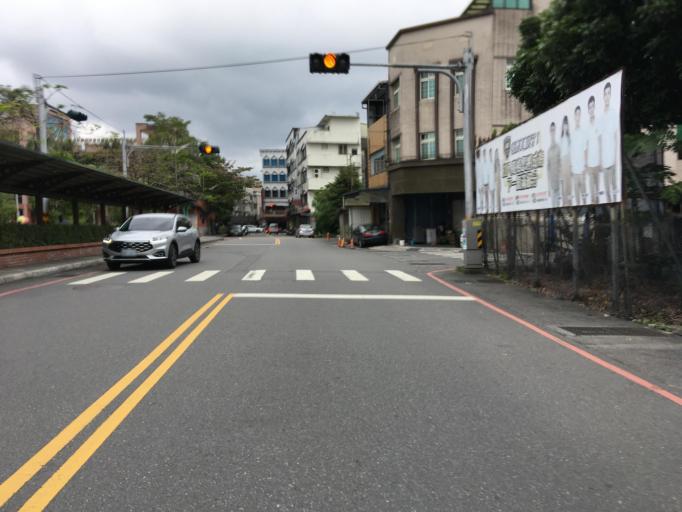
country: TW
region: Taiwan
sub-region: Yilan
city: Yilan
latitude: 24.6746
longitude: 121.7592
